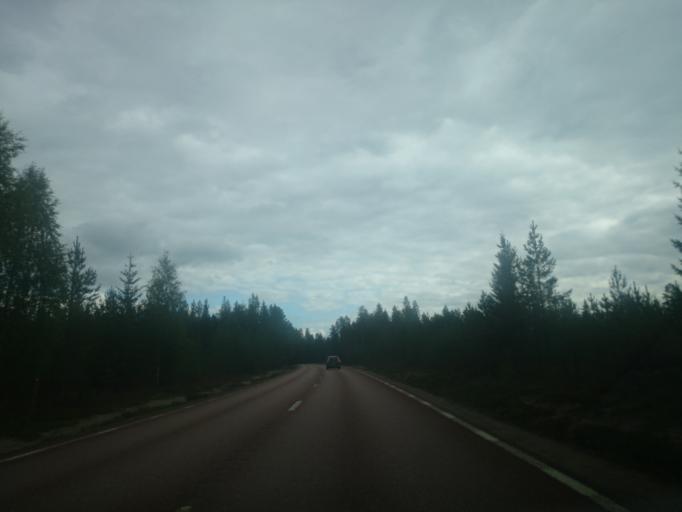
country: SE
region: Gaevleborg
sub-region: Ljusdals Kommun
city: Farila
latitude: 61.9209
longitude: 15.6080
